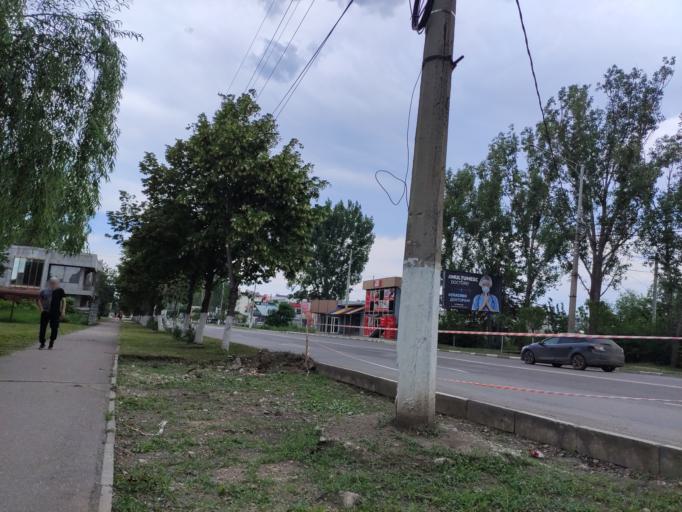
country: MD
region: Balti
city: Balti
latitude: 47.7612
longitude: 27.9408
